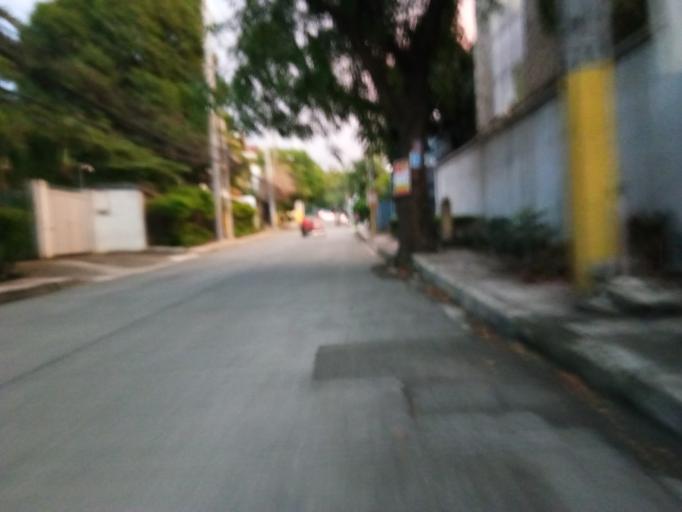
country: PH
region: Metro Manila
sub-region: San Juan
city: San Juan
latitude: 14.6121
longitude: 121.0479
